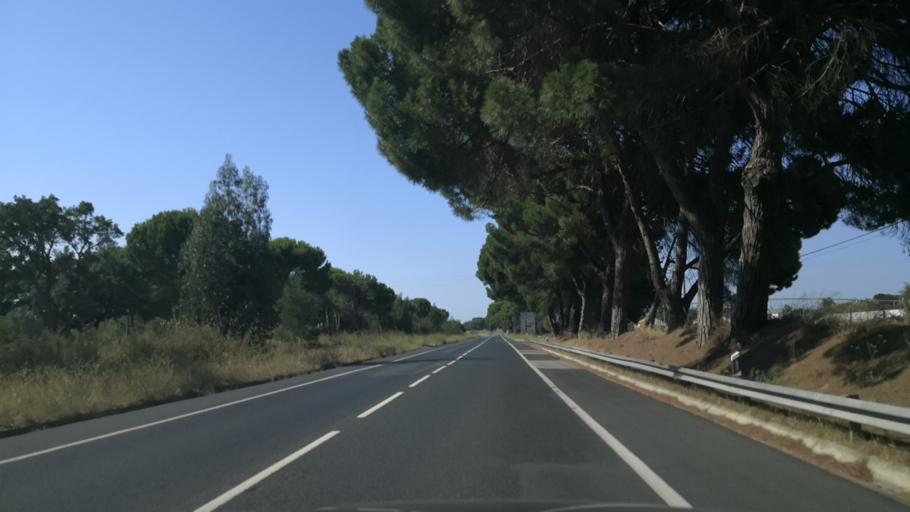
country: PT
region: Evora
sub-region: Vendas Novas
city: Vendas Novas
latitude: 38.7118
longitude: -8.6158
